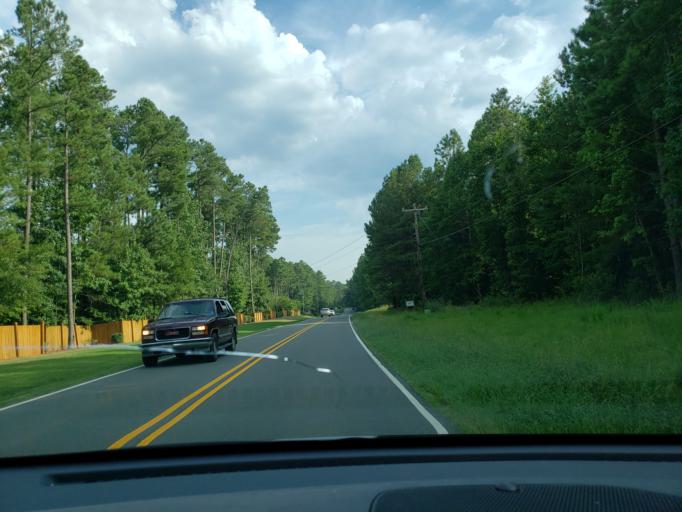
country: US
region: North Carolina
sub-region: Orange County
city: Chapel Hill
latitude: 35.8972
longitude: -78.9799
